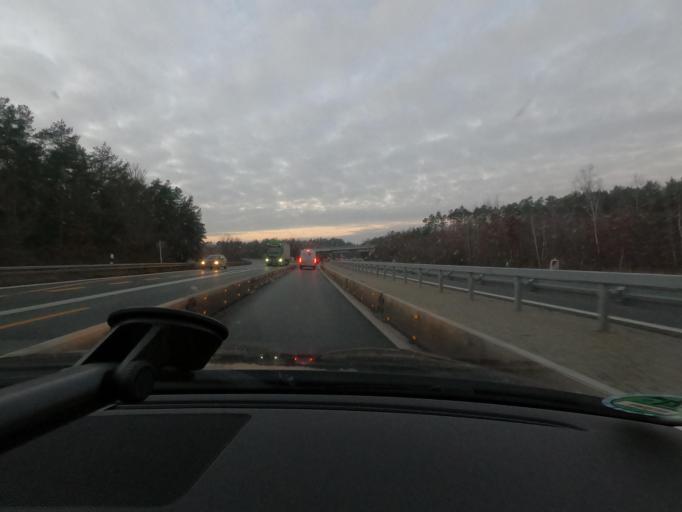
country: DE
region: Bavaria
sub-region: Upper Franconia
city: Strullendorf
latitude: 49.8690
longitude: 10.9519
